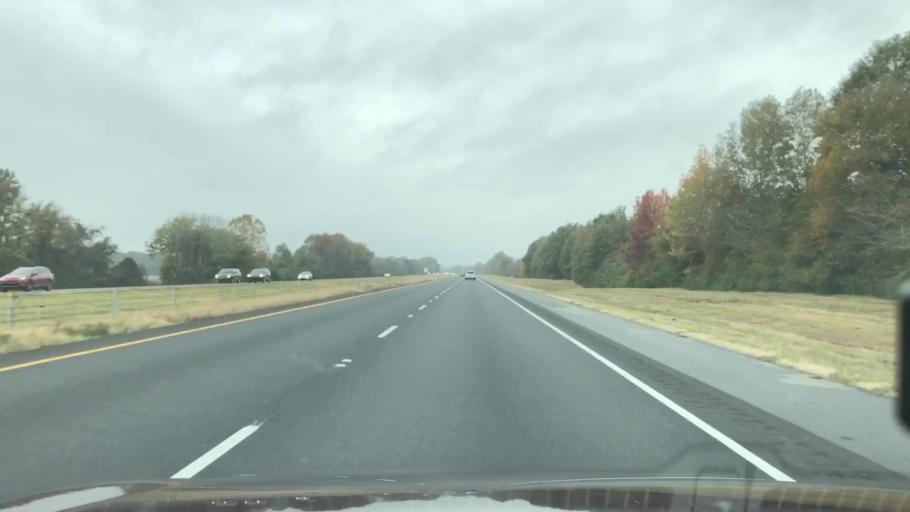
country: US
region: Louisiana
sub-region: Richland Parish
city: Rayville
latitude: 32.4624
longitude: -91.7860
